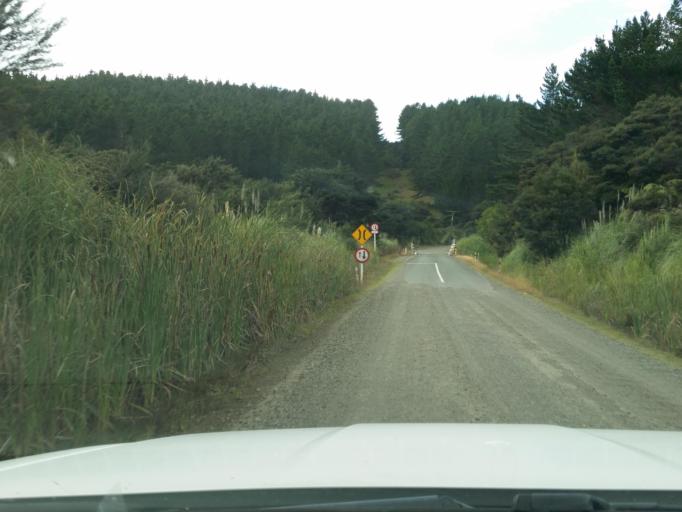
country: NZ
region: Auckland
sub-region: Auckland
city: Wellsford
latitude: -36.3059
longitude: 174.1194
